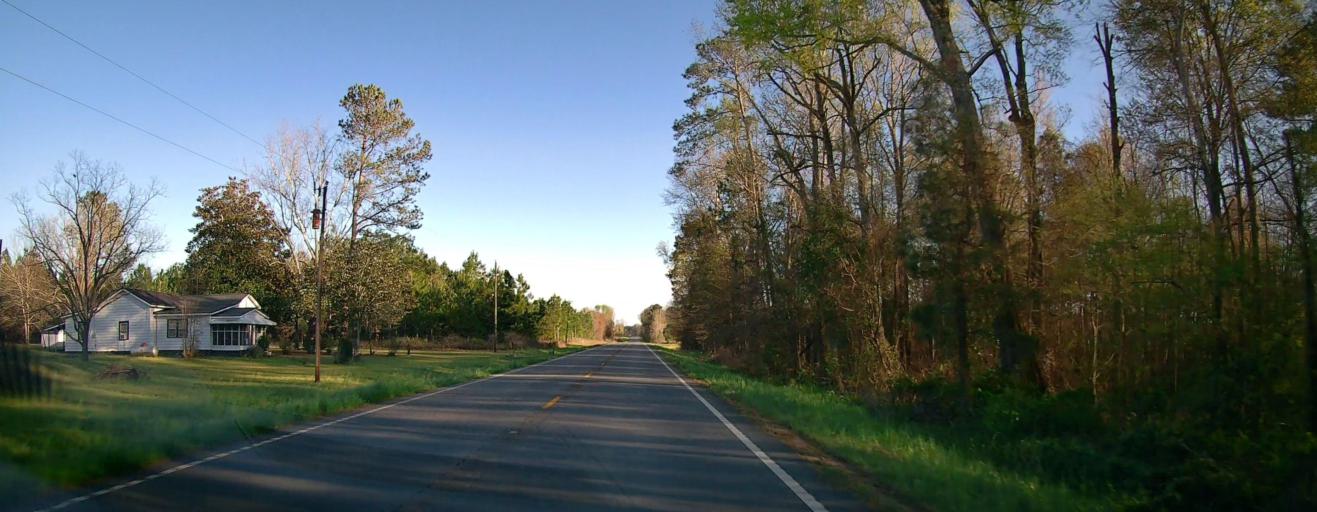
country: US
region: Georgia
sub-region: Pulaski County
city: Hawkinsville
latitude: 32.2287
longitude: -83.3941
